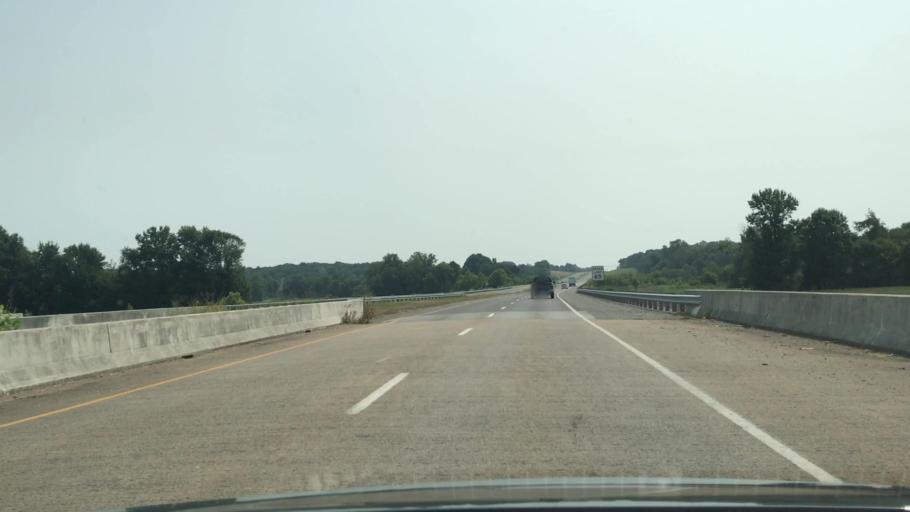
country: US
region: Kentucky
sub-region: Calloway County
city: Murray
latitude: 36.6518
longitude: -88.2879
